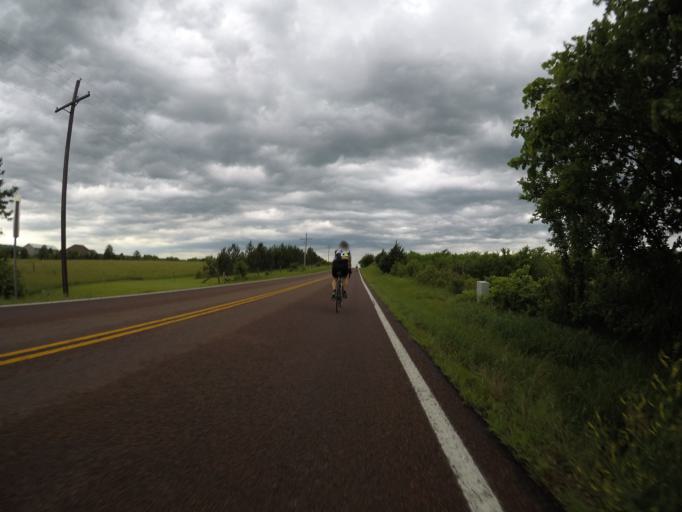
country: US
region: Kansas
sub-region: Shawnee County
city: Rossville
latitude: 38.9645
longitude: -95.9861
